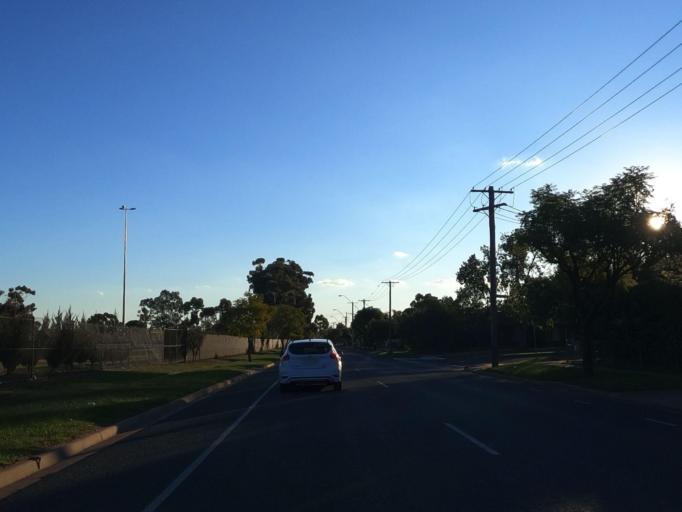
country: AU
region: Victoria
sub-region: Swan Hill
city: Swan Hill
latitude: -35.3480
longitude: 143.5581
